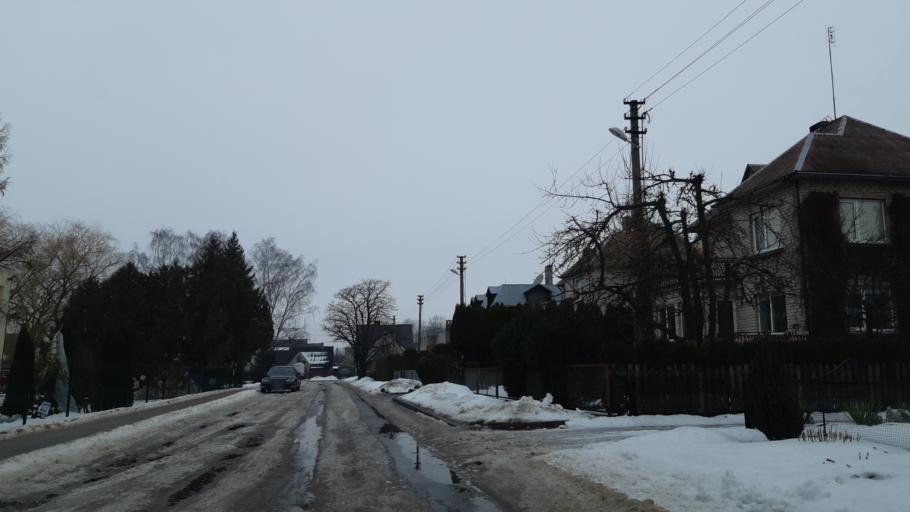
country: LT
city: Vilkaviskis
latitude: 54.6455
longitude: 23.0345
